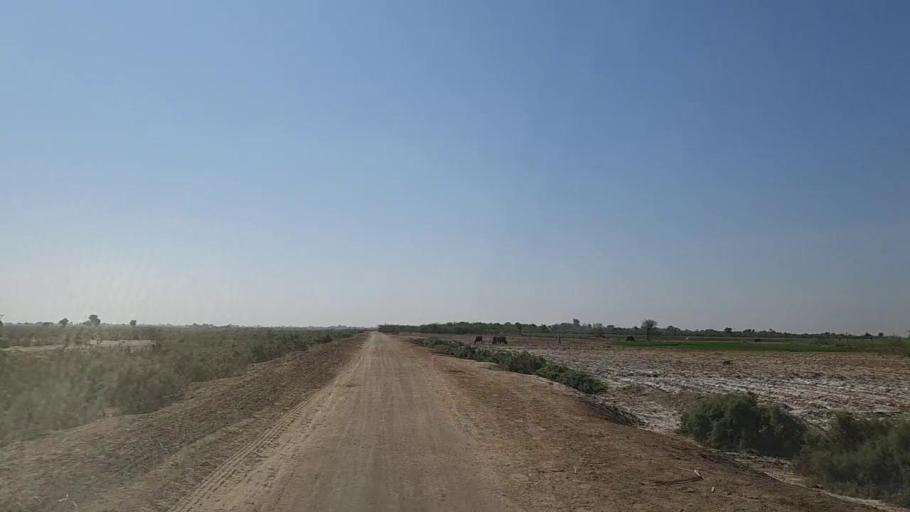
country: PK
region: Sindh
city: Pithoro
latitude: 25.4251
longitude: 69.3767
